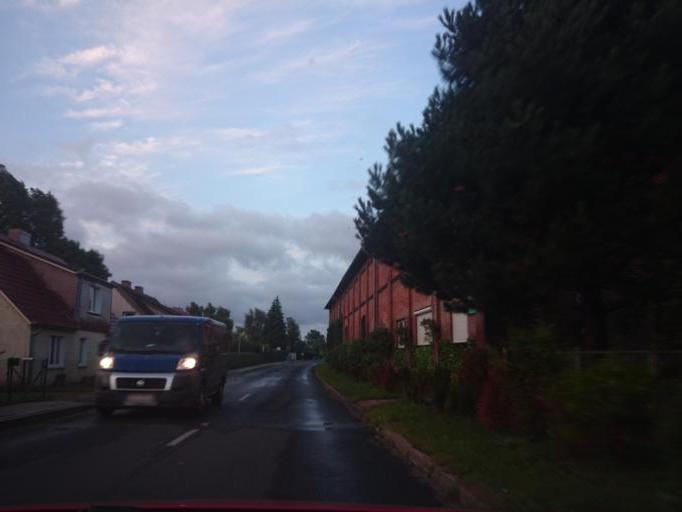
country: DE
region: Mecklenburg-Vorpommern
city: Velgast
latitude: 54.3310
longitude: 12.7966
